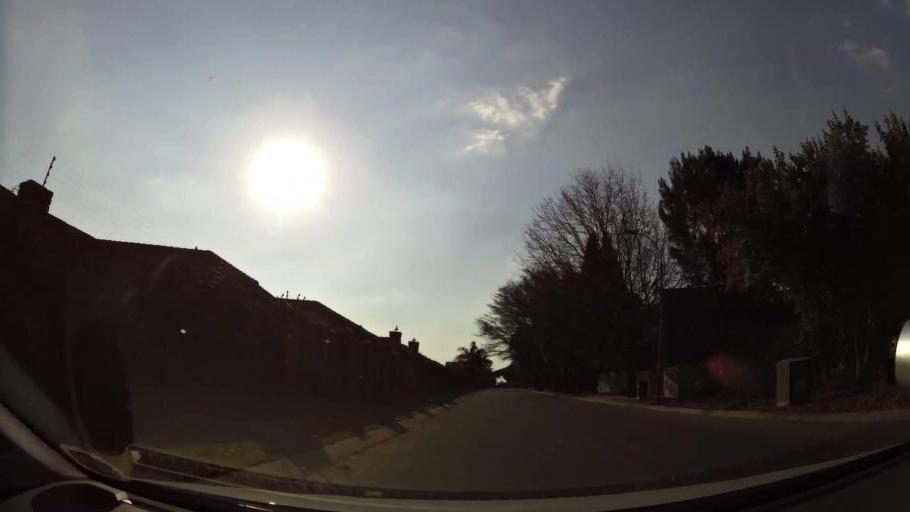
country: ZA
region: Gauteng
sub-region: City of Johannesburg Metropolitan Municipality
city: Modderfontein
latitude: -26.0765
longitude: 28.2042
